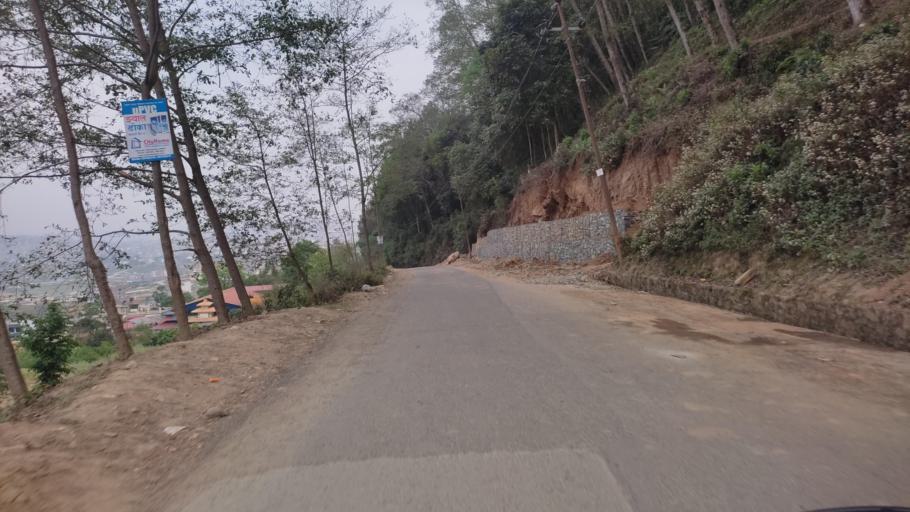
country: NP
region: Central Region
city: Kirtipur
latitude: 27.6680
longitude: 85.2458
